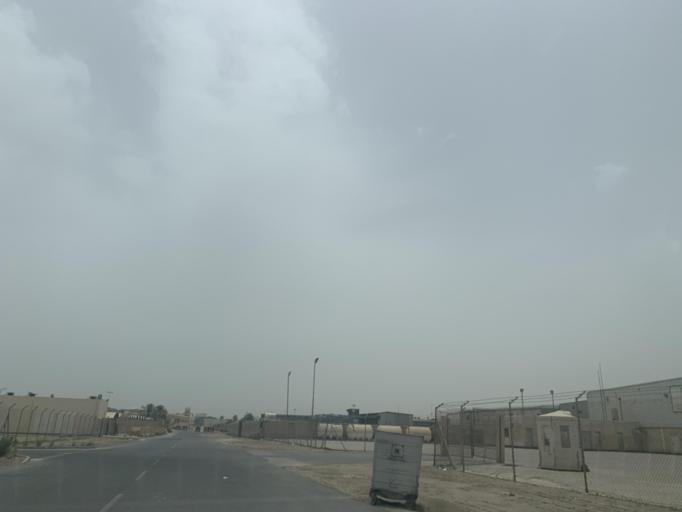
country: BH
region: Northern
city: Sitrah
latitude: 26.1773
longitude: 50.6256
